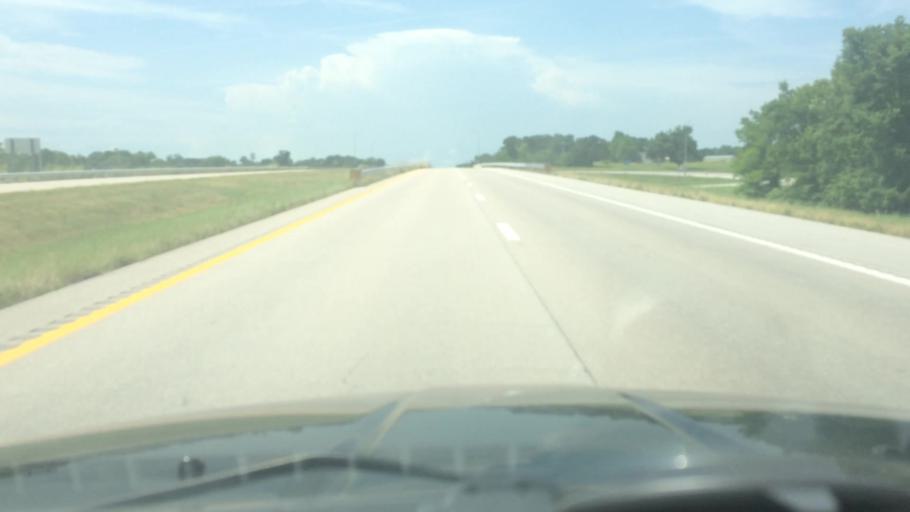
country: US
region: Missouri
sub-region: Polk County
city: Humansville
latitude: 37.7927
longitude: -93.5870
